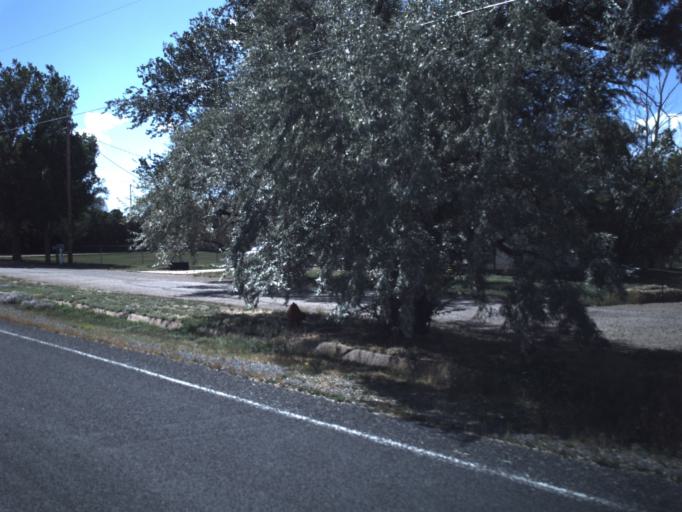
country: US
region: Utah
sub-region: Iron County
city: Enoch
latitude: 37.7451
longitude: -113.0553
